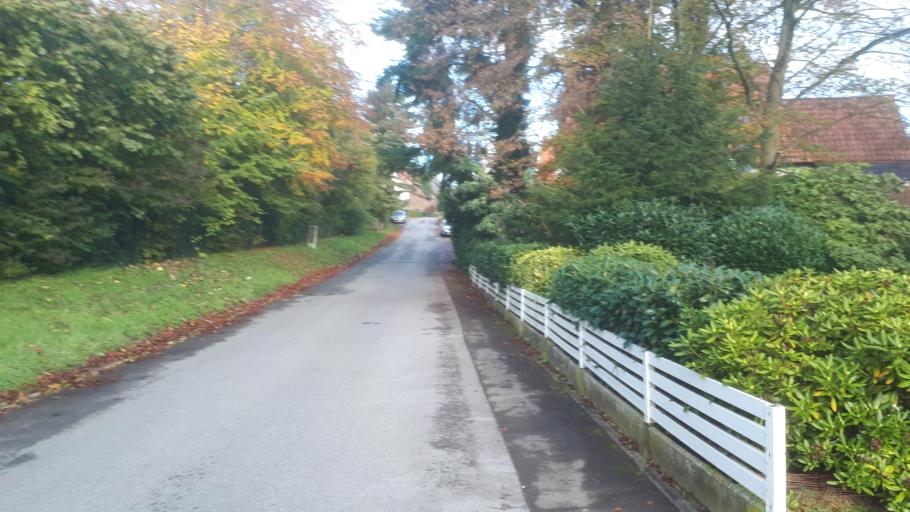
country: DE
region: North Rhine-Westphalia
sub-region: Regierungsbezirk Detmold
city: Huellhorst
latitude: 52.2733
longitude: 8.7075
